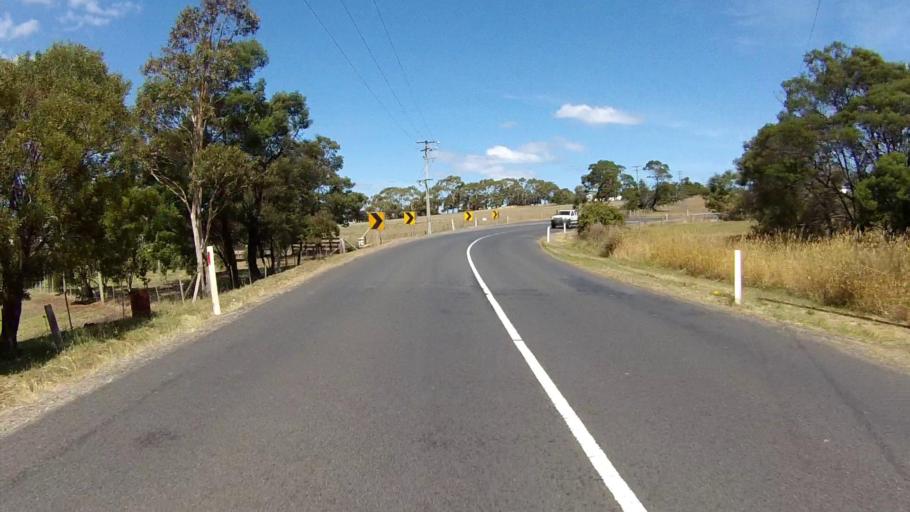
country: AU
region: Tasmania
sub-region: Sorell
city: Sorell
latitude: -42.7809
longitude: 147.5241
